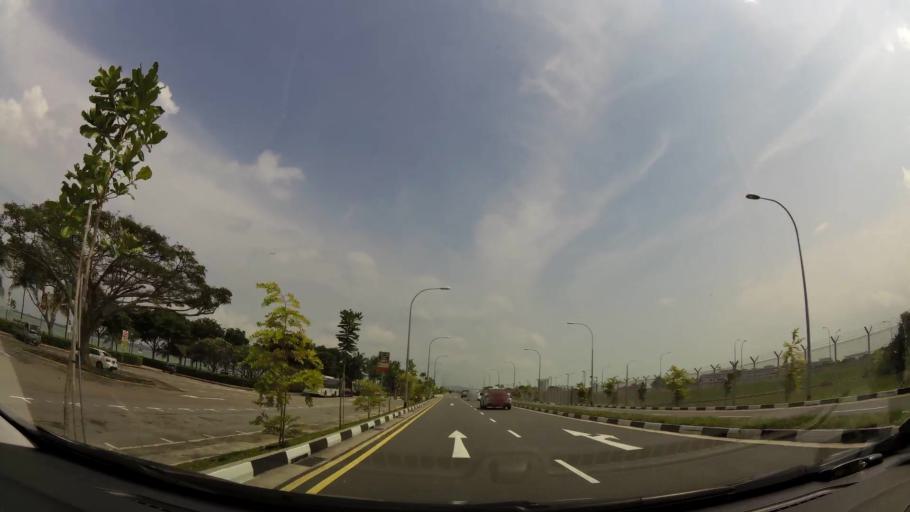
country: MY
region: Johor
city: Kampung Pasir Gudang Baru
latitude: 1.3899
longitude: 103.9939
